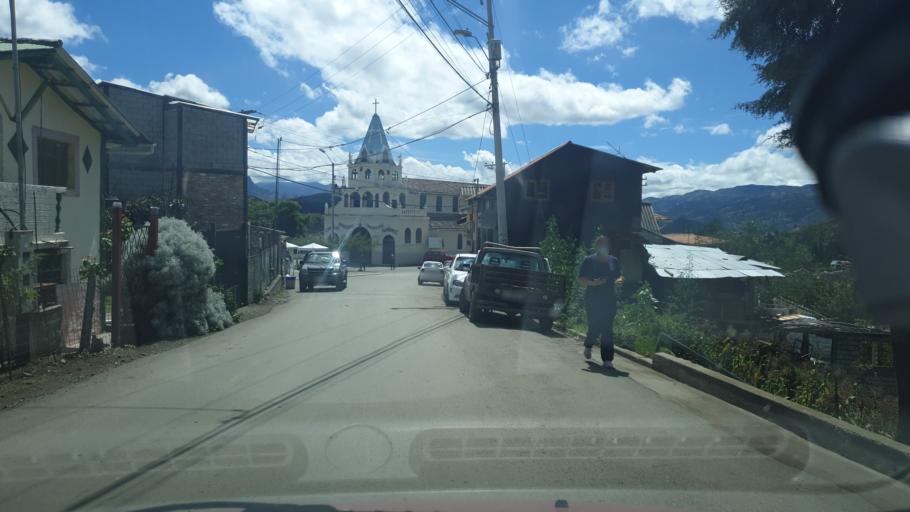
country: EC
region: Azuay
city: Llacao
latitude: -2.8639
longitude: -78.9076
